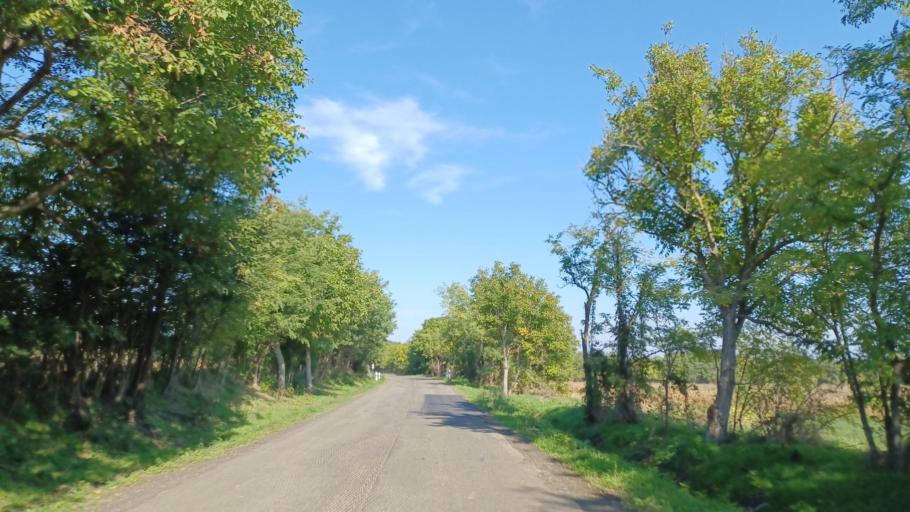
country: HU
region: Tolna
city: Nagydorog
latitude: 46.5907
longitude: 18.5964
